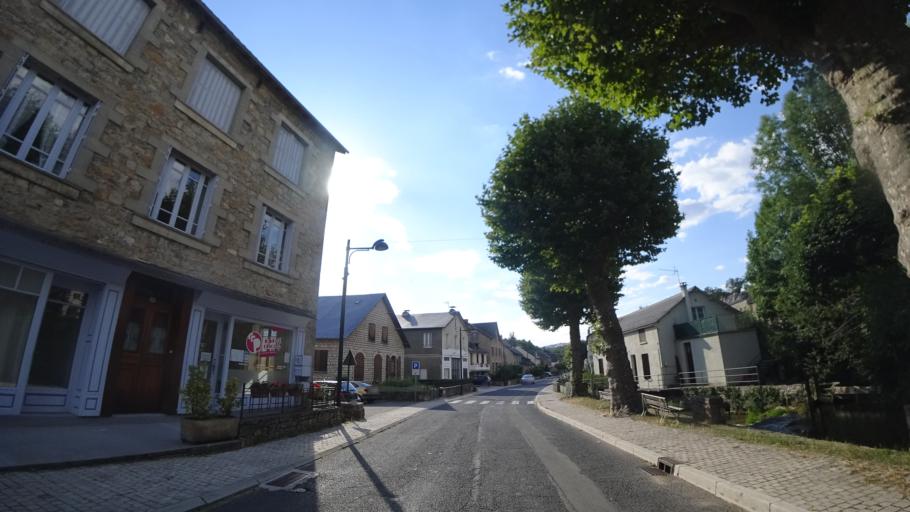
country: FR
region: Languedoc-Roussillon
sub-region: Departement de la Lozere
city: La Canourgue
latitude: 44.4296
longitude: 3.2176
